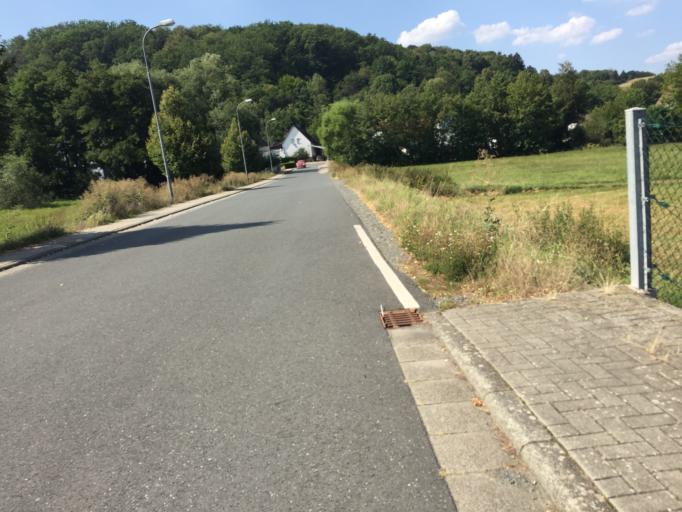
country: DE
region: Hesse
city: Solms
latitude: 50.5214
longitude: 8.4106
